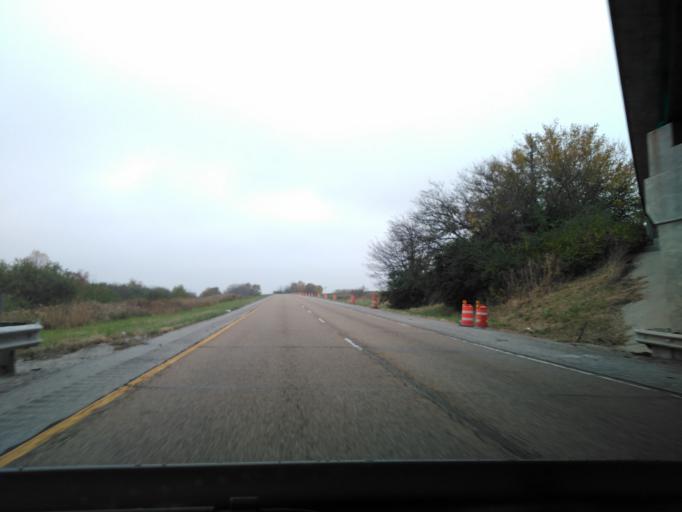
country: US
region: Illinois
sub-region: Madison County
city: Troy
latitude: 38.7513
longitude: -89.9026
